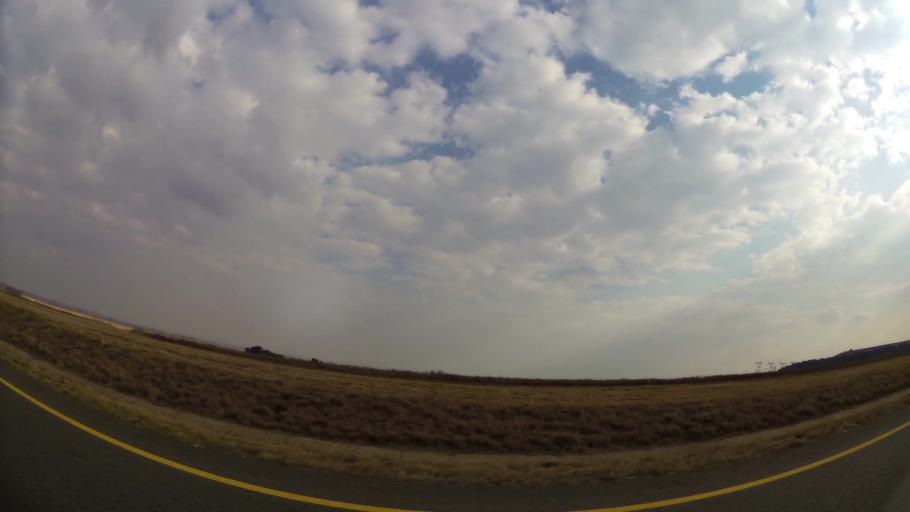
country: ZA
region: Gauteng
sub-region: Ekurhuleni Metropolitan Municipality
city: Nigel
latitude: -26.3006
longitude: 28.5583
